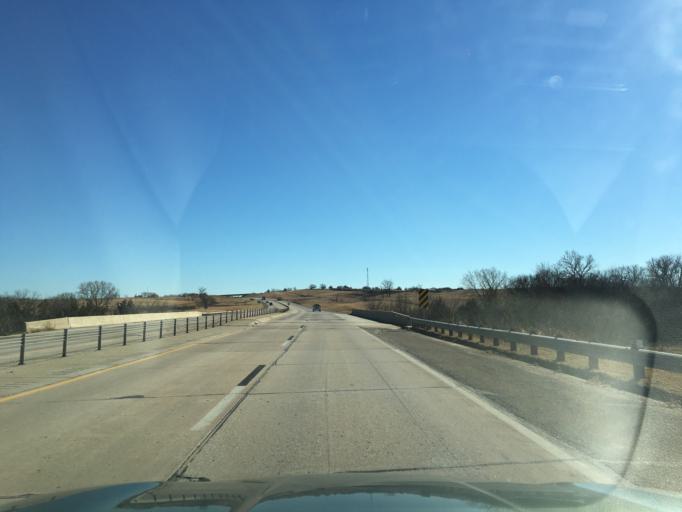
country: US
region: Oklahoma
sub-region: Payne County
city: Stillwater
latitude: 36.2542
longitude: -96.9694
